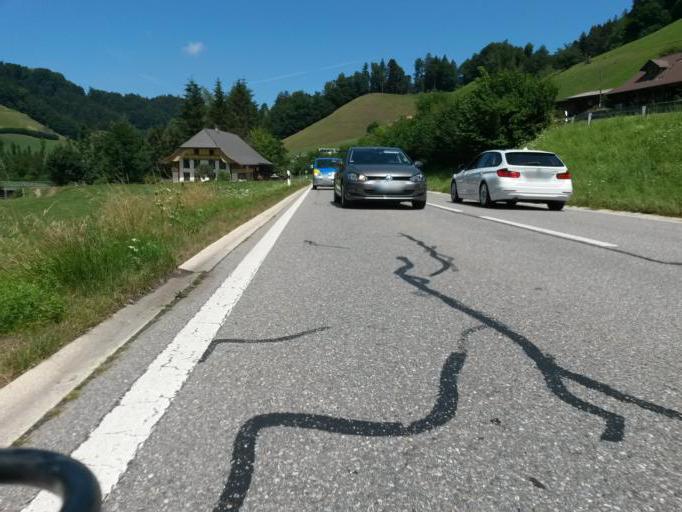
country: CH
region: Bern
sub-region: Bern-Mittelland District
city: Walkringen
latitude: 46.9603
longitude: 7.6228
